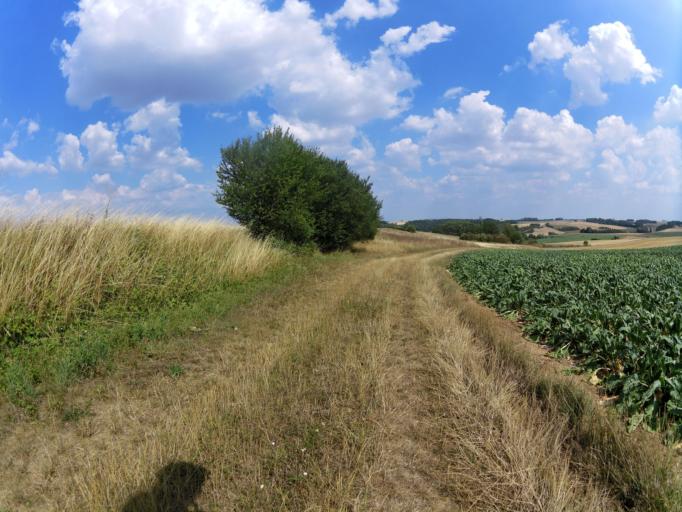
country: DE
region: Bavaria
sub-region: Regierungsbezirk Unterfranken
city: Ochsenfurt
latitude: 49.6484
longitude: 10.0713
